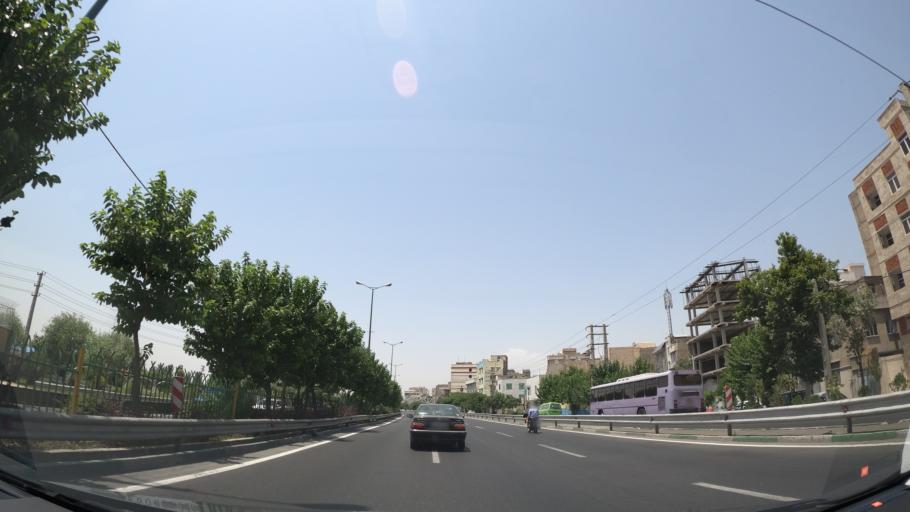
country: IR
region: Tehran
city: Tehran
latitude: 35.6506
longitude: 51.3880
